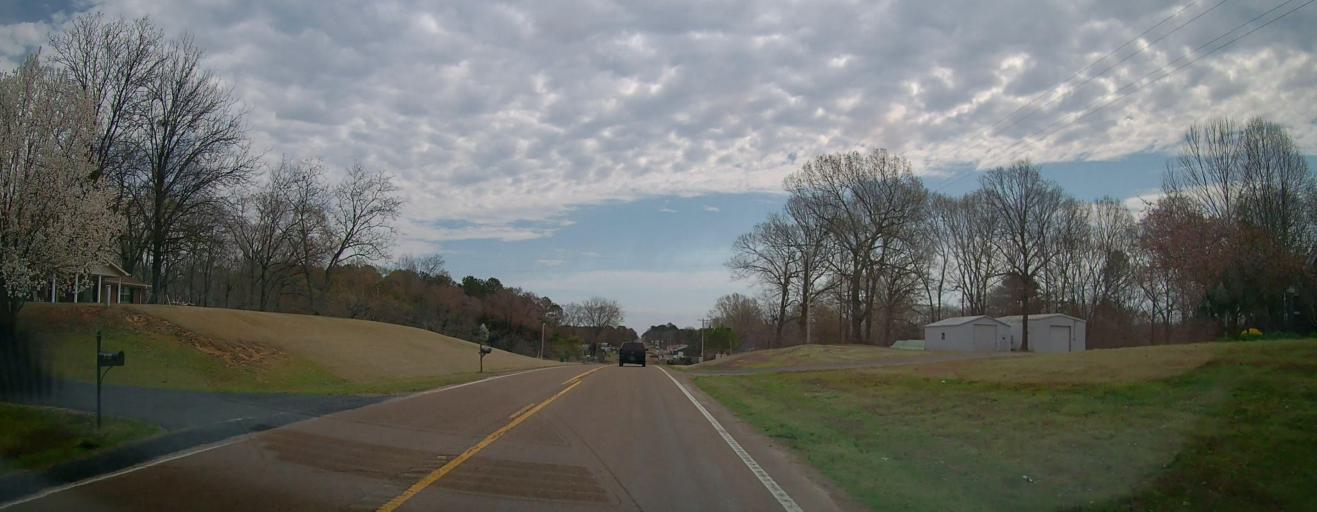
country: US
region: Mississippi
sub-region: Marshall County
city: Byhalia
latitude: 34.8308
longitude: -89.5728
